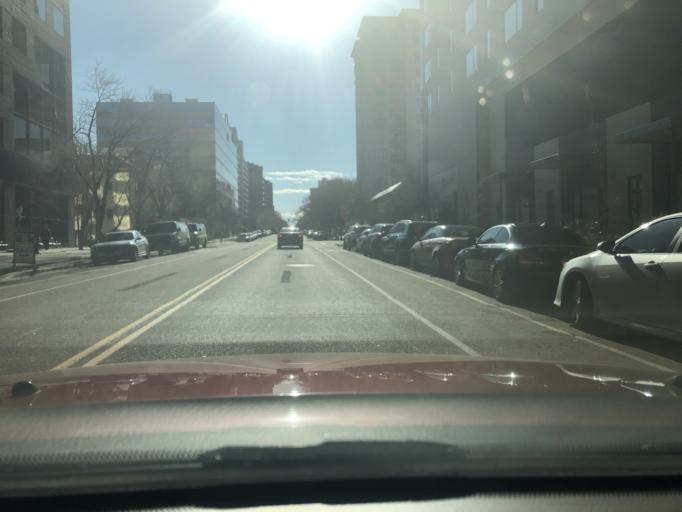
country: US
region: Colorado
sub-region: Denver County
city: Denver
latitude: 39.7468
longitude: -104.9836
